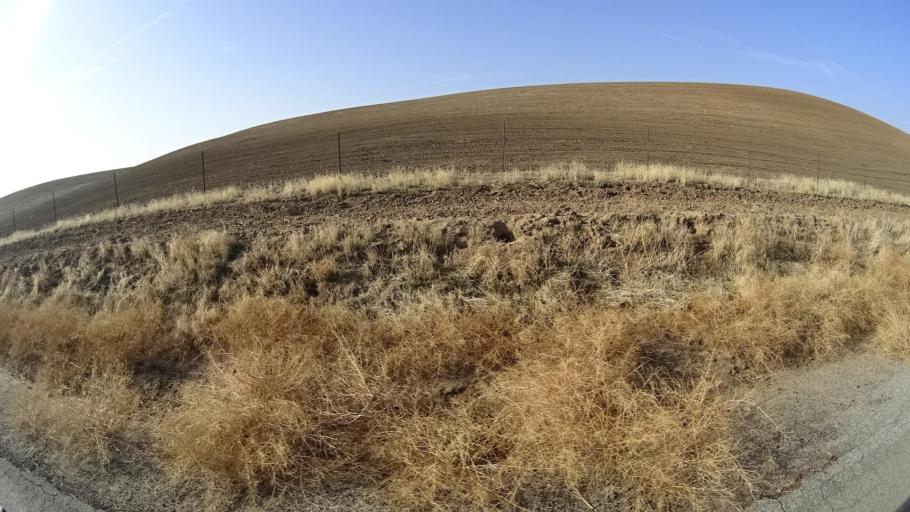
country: US
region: California
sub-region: Tulare County
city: Richgrove
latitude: 35.6556
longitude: -119.0688
